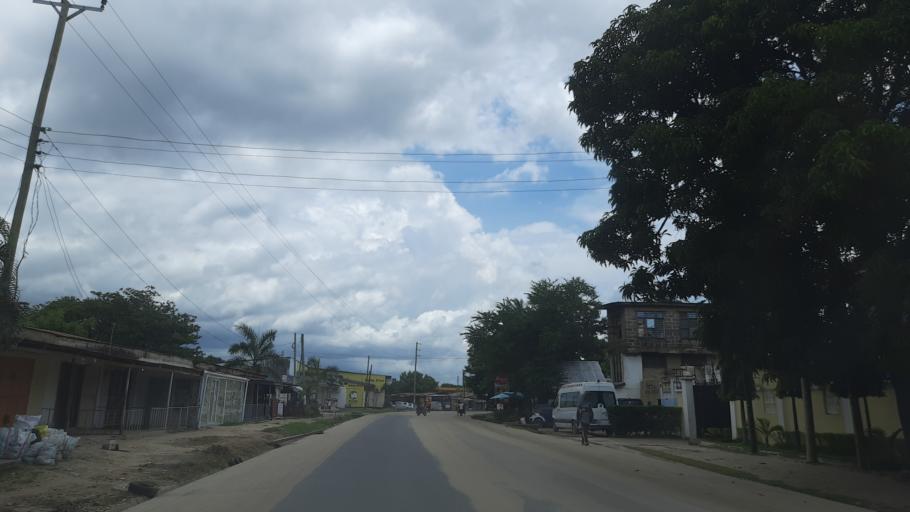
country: TZ
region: Dar es Salaam
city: Magomeni
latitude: -6.7763
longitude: 39.2342
